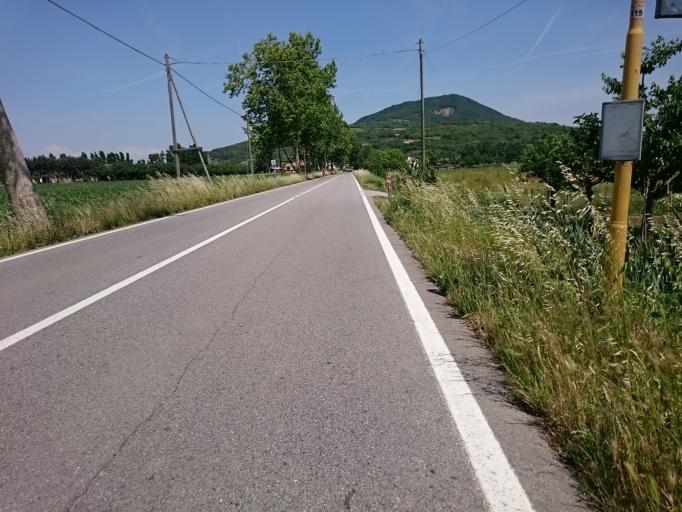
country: IT
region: Veneto
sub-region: Provincia di Padova
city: Lozzo Atestino
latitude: 45.2746
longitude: 11.6162
